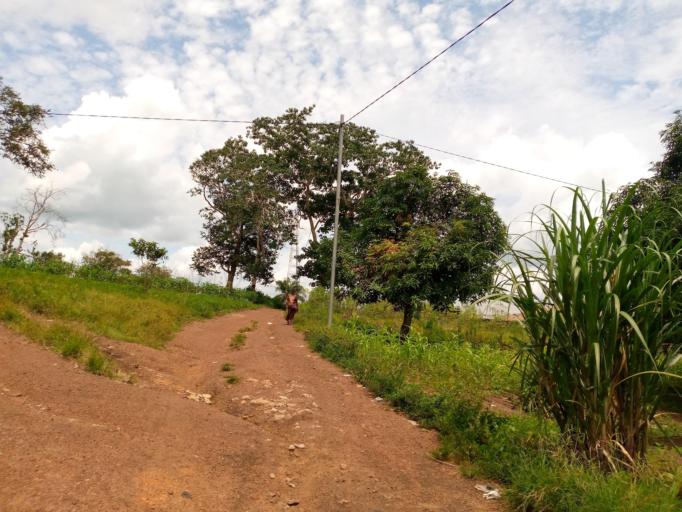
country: SL
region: Northern Province
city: Magburaka
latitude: 8.7242
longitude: -11.9354
